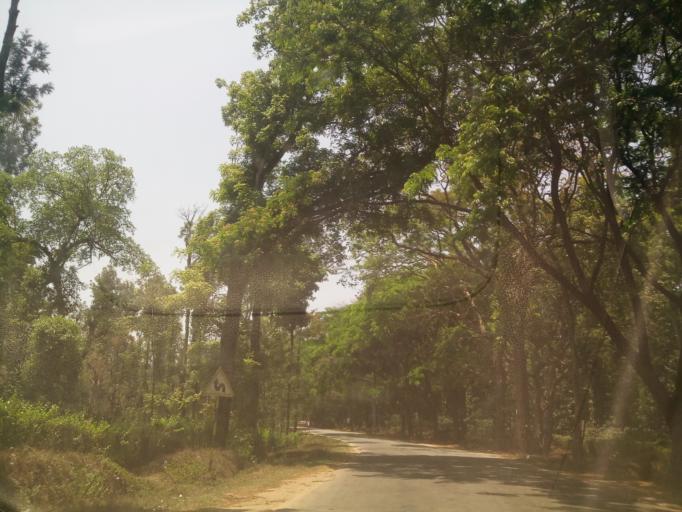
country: IN
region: Karnataka
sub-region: Hassan
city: Sakleshpur
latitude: 12.9531
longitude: 75.8254
